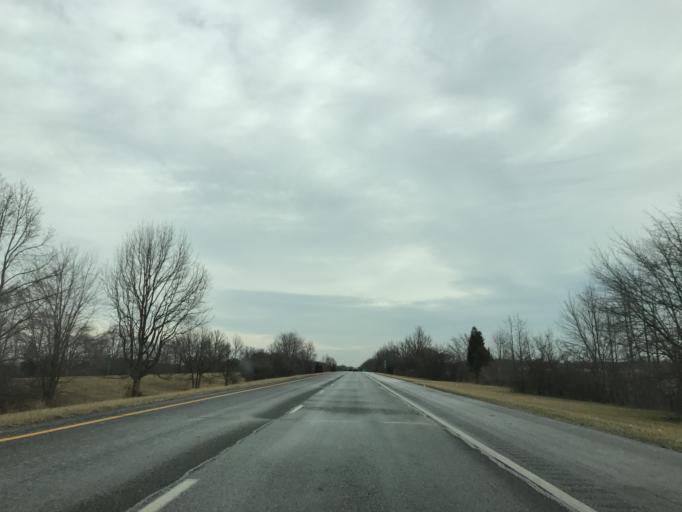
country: US
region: New Jersey
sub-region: Salem County
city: Penns Grove
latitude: 39.7231
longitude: -75.4216
